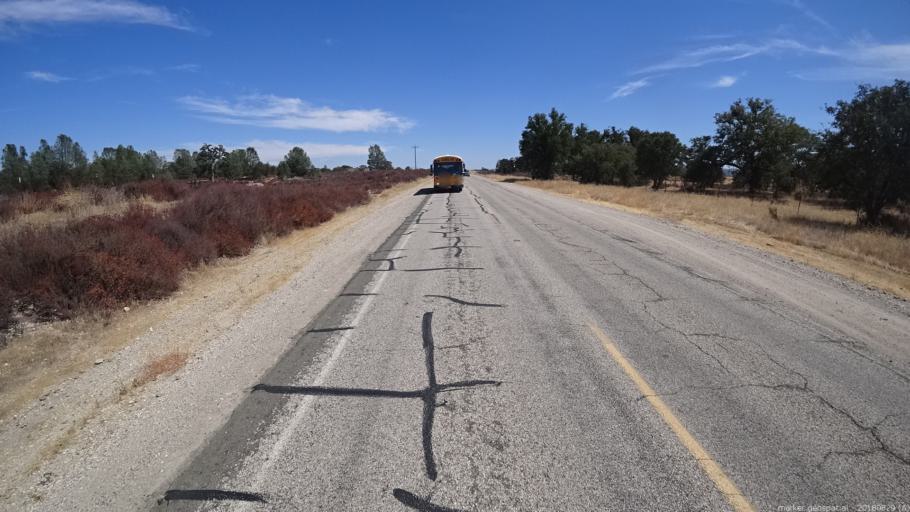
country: US
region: California
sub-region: Monterey County
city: King City
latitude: 35.9653
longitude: -121.1710
